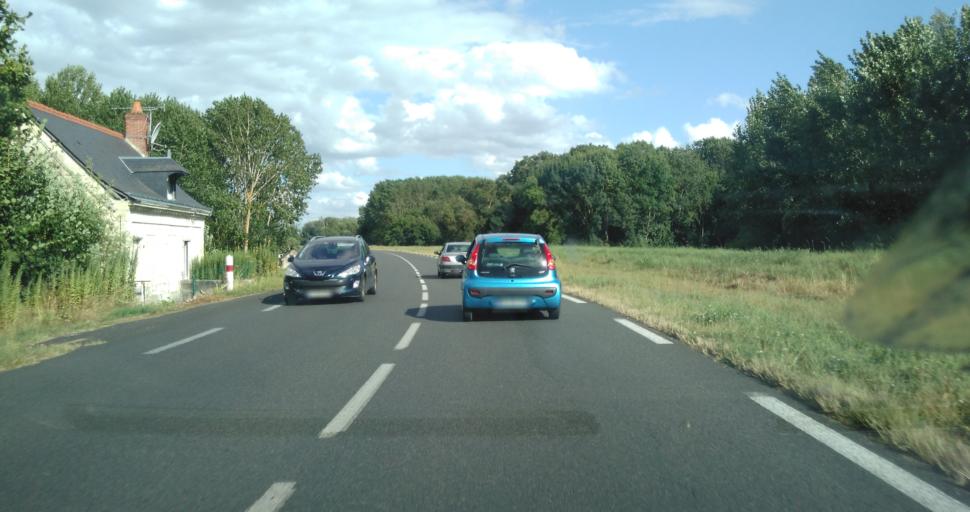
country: FR
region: Centre
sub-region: Departement d'Indre-et-Loire
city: Avoine
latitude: 47.2404
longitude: 0.1731
